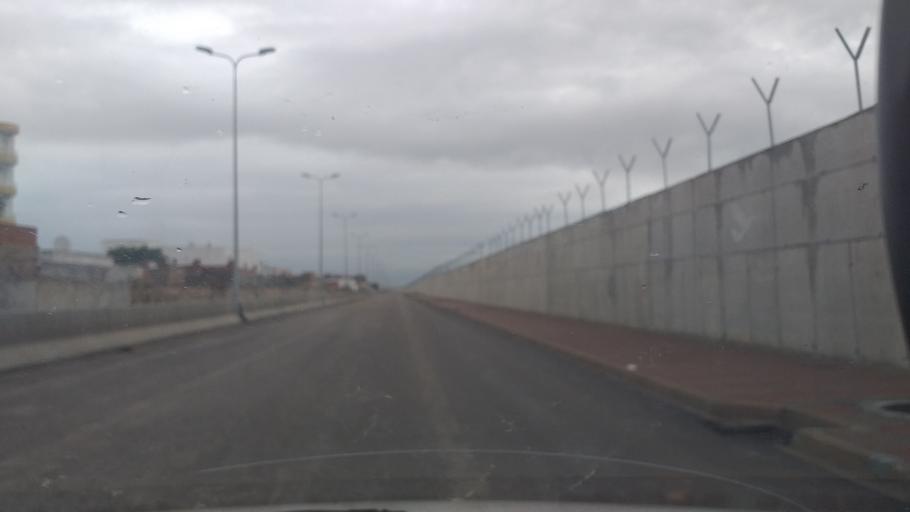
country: TN
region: Ariana
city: Ariana
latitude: 36.8618
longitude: 10.2179
